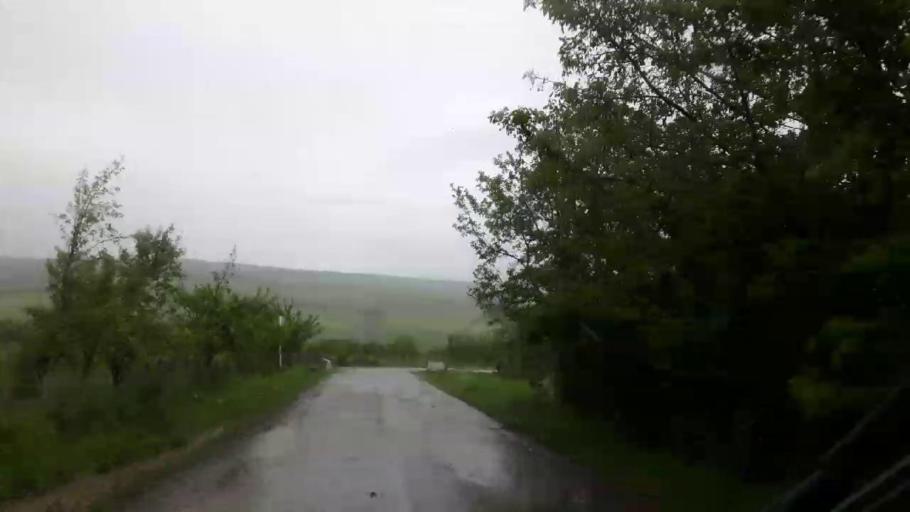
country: GE
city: Agara
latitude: 42.0037
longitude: 43.7585
